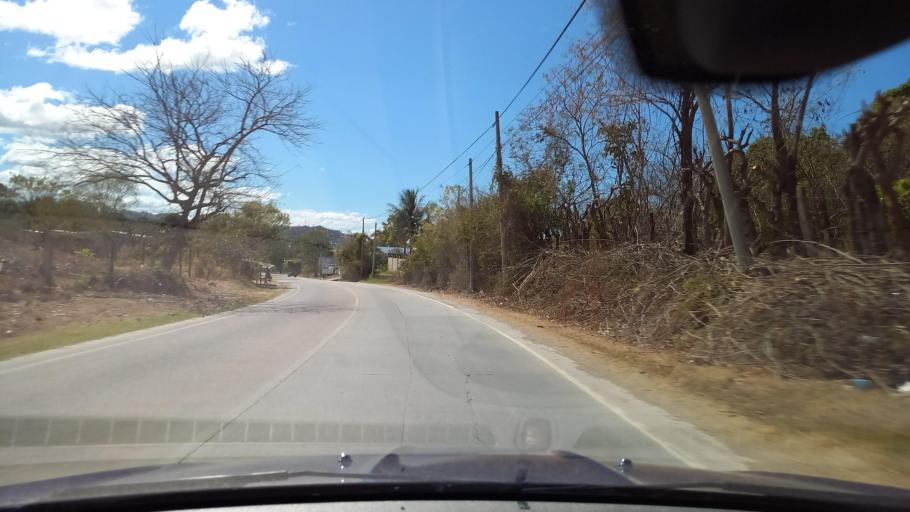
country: SV
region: Santa Ana
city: Metapan
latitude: 14.3575
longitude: -89.4541
